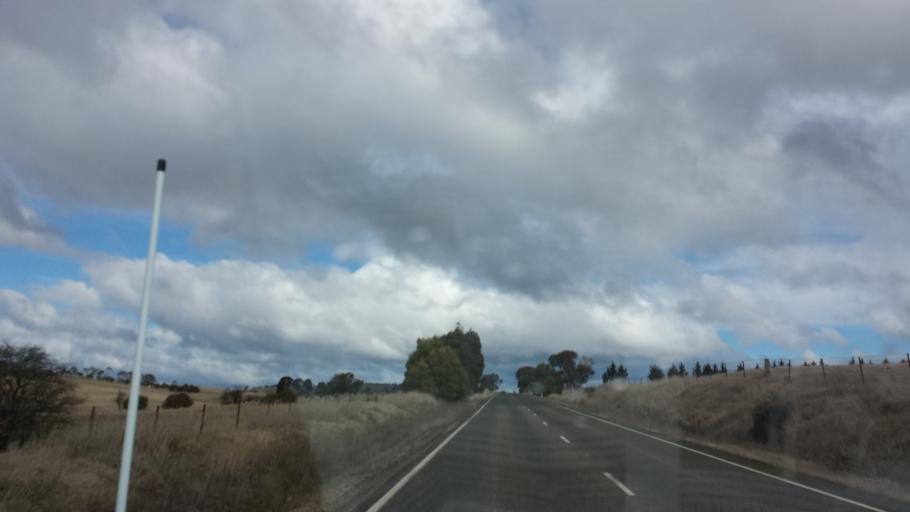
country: AU
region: Victoria
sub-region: Alpine
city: Mount Beauty
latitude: -37.1344
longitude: 147.6457
